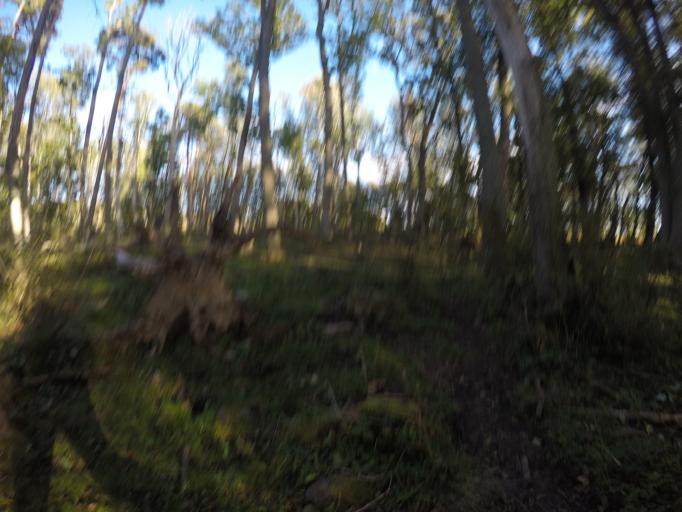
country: SE
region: Soedermanland
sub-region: Eskilstuna Kommun
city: Kvicksund
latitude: 59.4776
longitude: 16.2426
